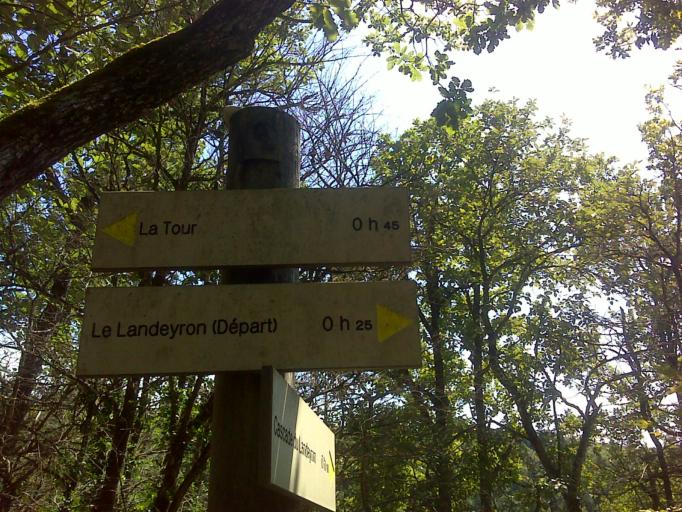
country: FR
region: Rhone-Alpes
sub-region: Departement de l'Ain
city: Montreal-la-Cluse
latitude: 46.1706
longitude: 5.6001
